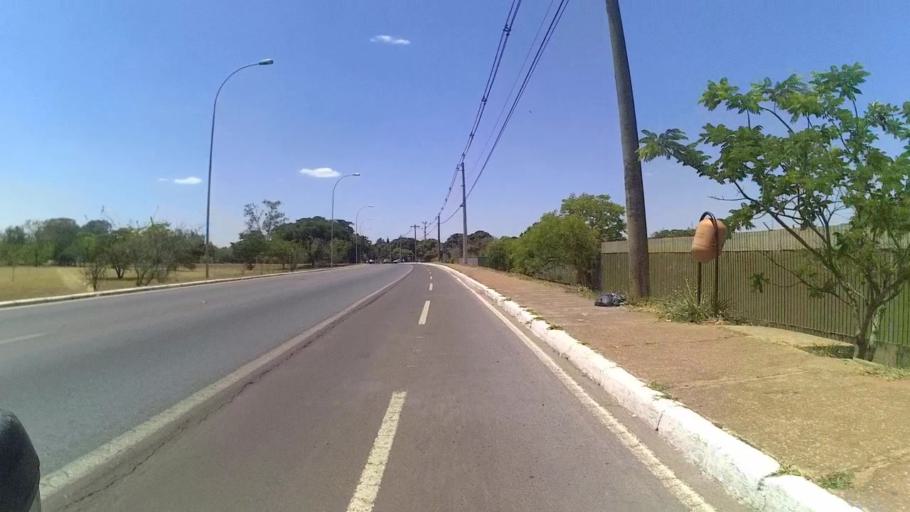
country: BR
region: Federal District
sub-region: Brasilia
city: Brasilia
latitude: -15.7400
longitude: -47.8582
